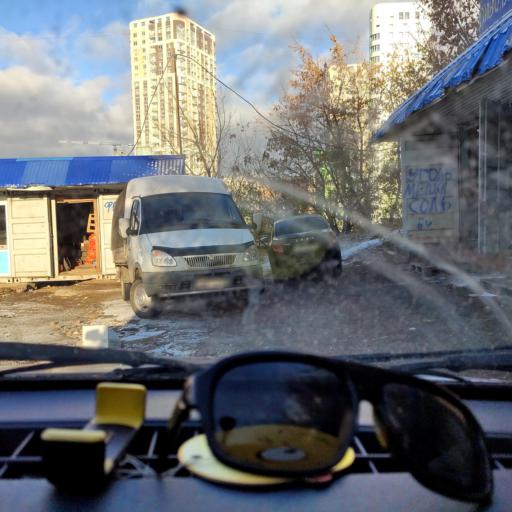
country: RU
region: Bashkortostan
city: Ufa
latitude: 54.7151
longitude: 55.9837
